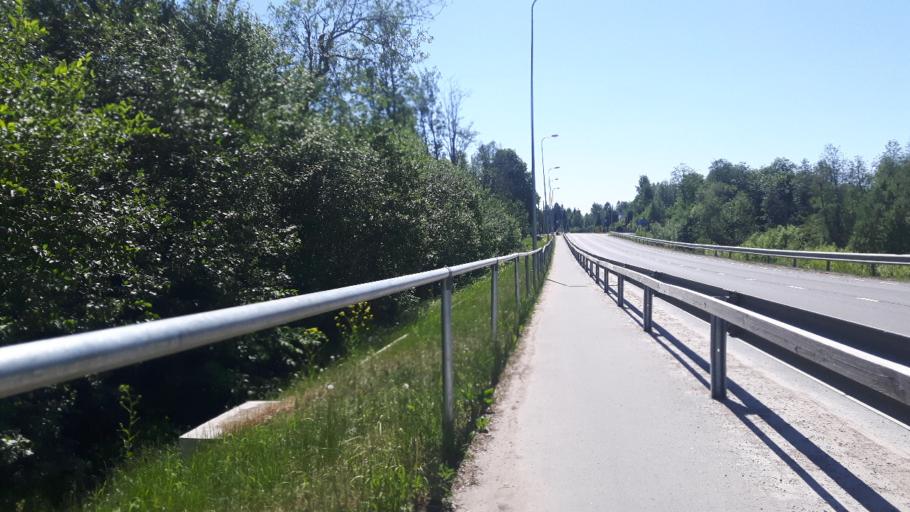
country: EE
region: Harju
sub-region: Saku vald
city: Saku
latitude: 59.2335
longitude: 24.6819
